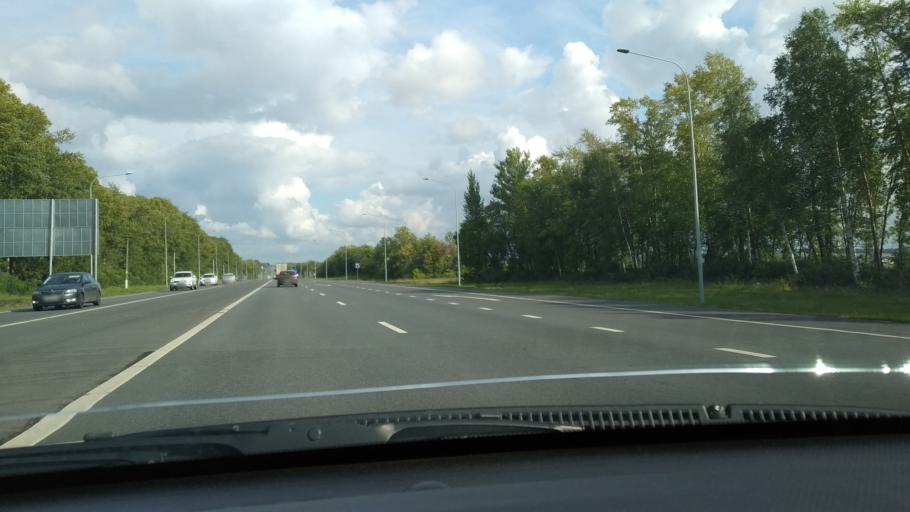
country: RU
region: Tatarstan
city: Stolbishchi
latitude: 55.6596
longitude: 49.3021
